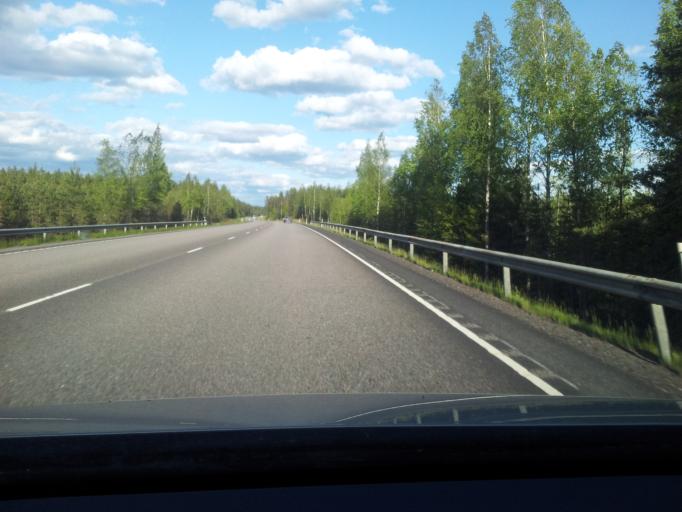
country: FI
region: Kymenlaakso
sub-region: Kouvola
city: Anjala
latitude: 60.9061
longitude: 27.0644
